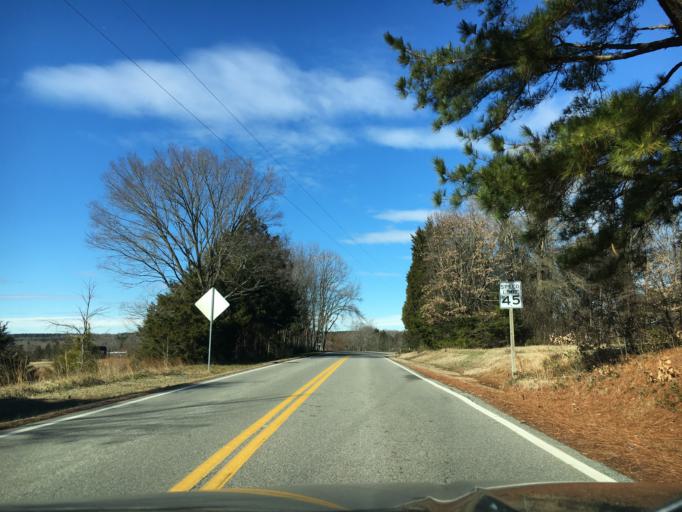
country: US
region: Virginia
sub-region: Halifax County
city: South Boston
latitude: 36.7195
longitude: -78.8618
